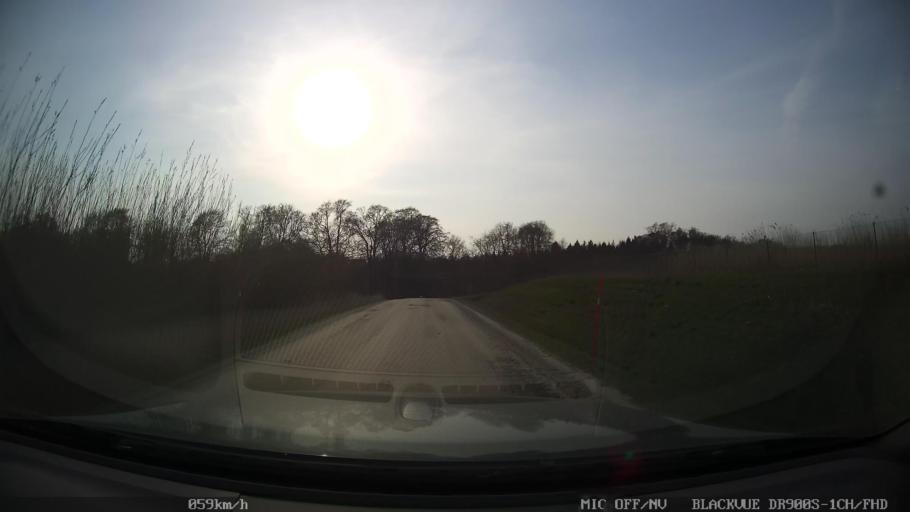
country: SE
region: Skane
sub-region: Ystads Kommun
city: Ystad
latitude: 55.4597
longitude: 13.7843
